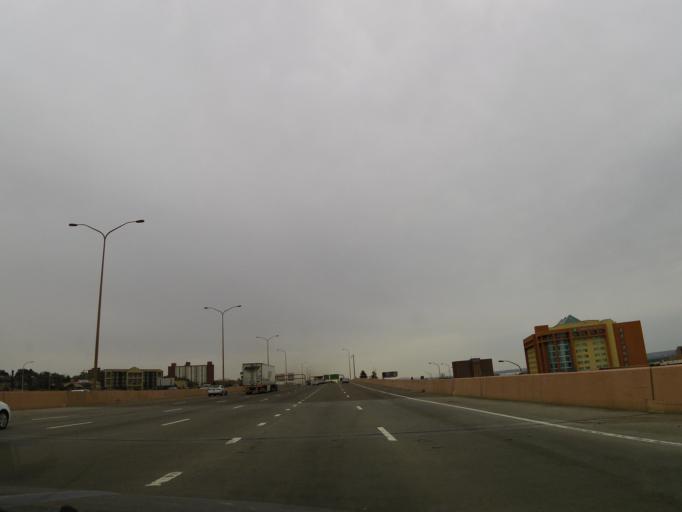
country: US
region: New Mexico
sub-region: Bernalillo County
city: Albuquerque
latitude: 35.0937
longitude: -106.6337
